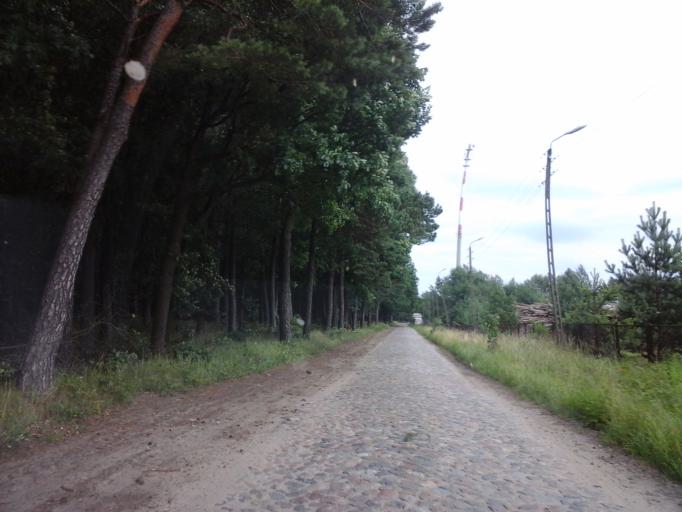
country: PL
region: Lubusz
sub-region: Powiat strzelecko-drezdenecki
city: Dobiegniew
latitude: 53.0912
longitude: 15.7931
